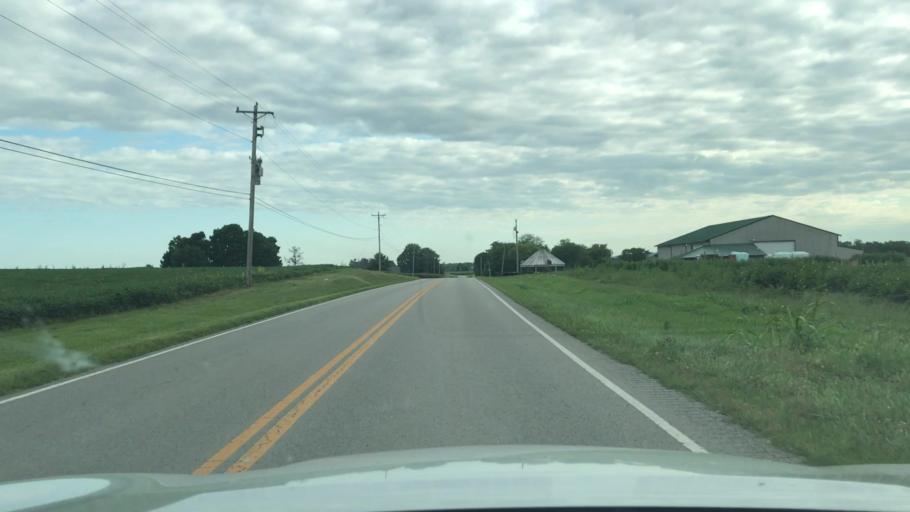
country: US
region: Kentucky
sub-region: Todd County
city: Elkton
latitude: 36.7723
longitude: -87.1664
